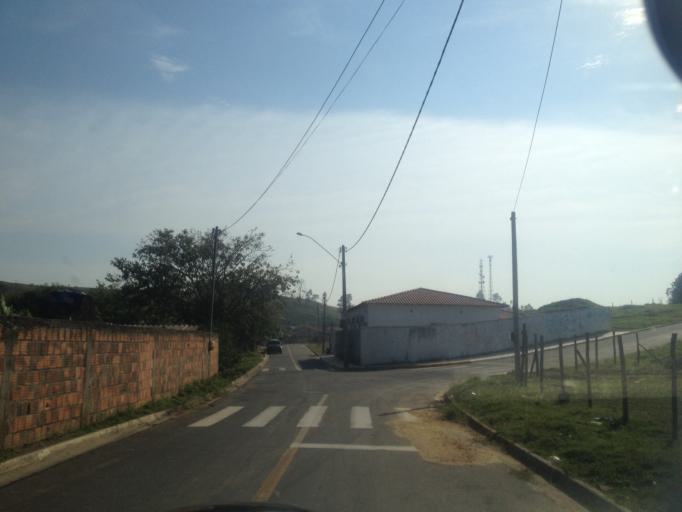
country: BR
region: Rio de Janeiro
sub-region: Porto Real
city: Porto Real
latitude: -22.4421
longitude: -44.3266
